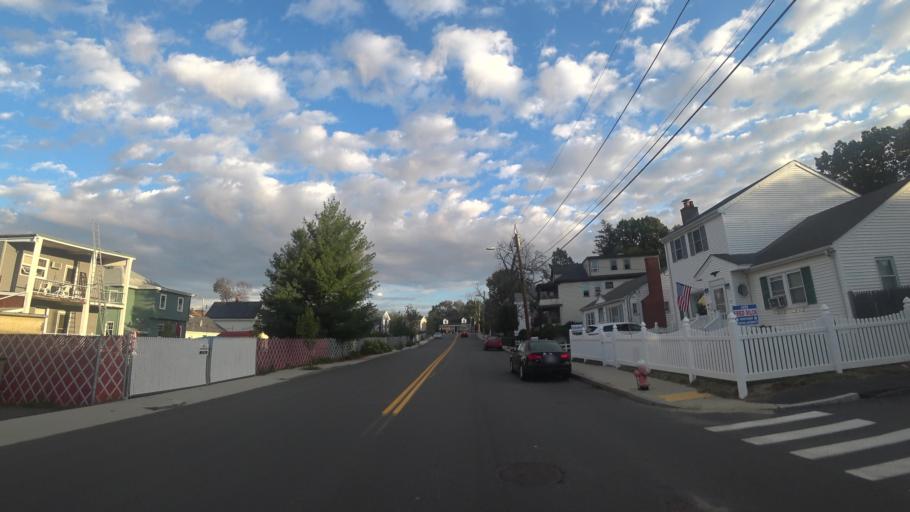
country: US
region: Massachusetts
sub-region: Suffolk County
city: Winthrop
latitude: 42.3806
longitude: -70.9869
